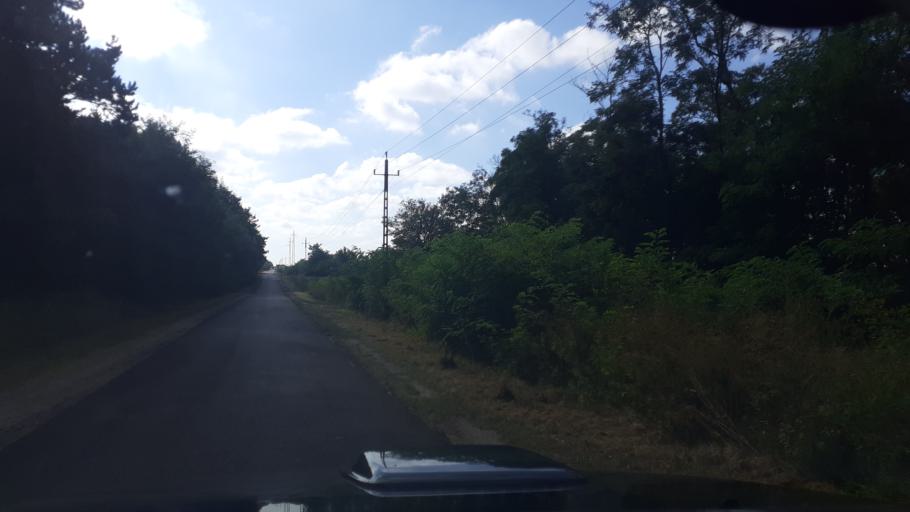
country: HU
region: Fejer
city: Baracs
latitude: 46.9394
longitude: 18.8663
